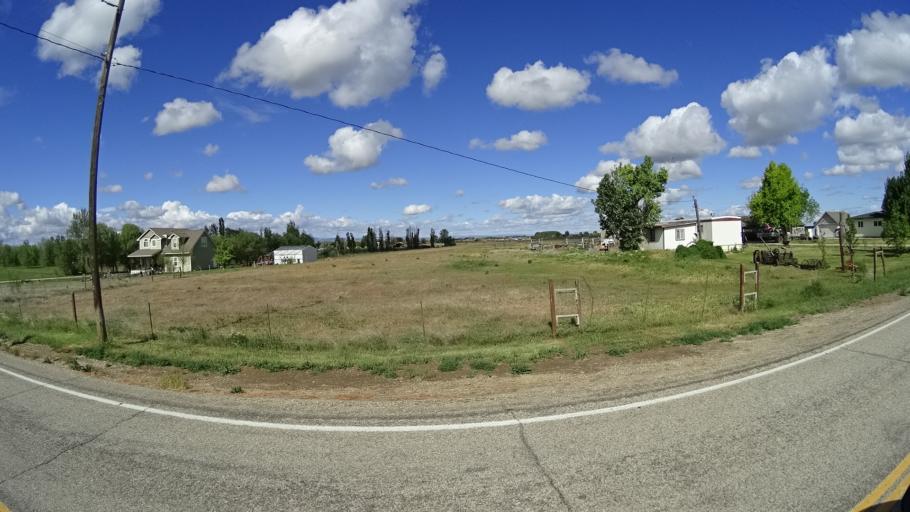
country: US
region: Idaho
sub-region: Ada County
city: Kuna
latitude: 43.4981
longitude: -116.4734
